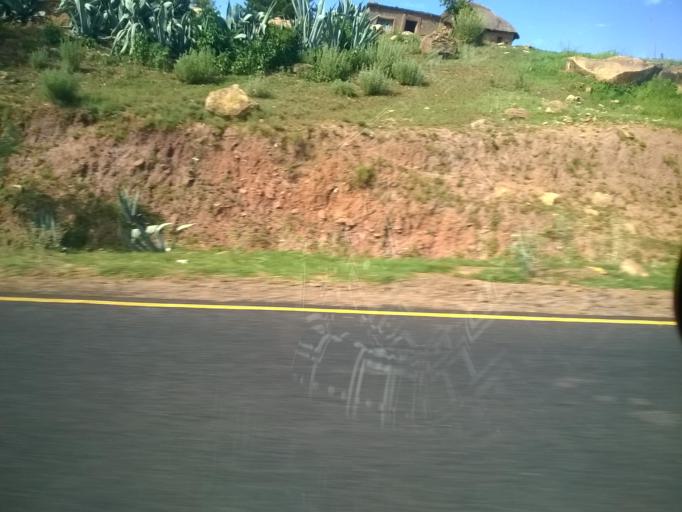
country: LS
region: Berea
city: Teyateyaneng
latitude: -29.0881
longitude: 27.9283
